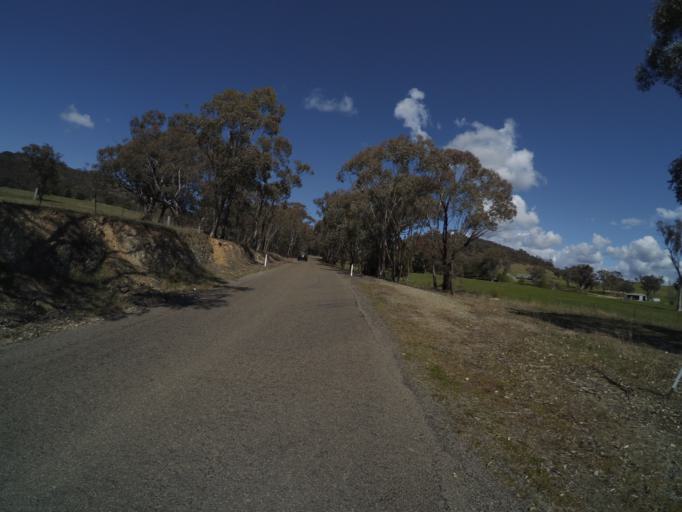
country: AU
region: New South Wales
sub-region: Yass Valley
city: Murrumbateman
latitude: -35.0772
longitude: 148.8401
